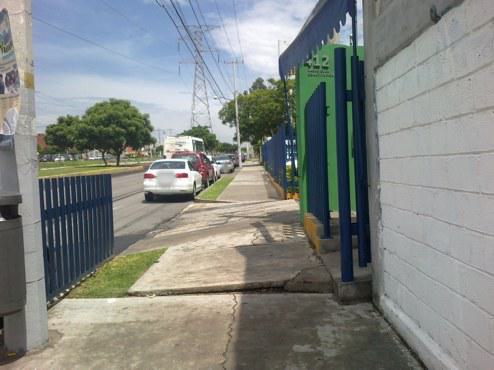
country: MX
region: Queretaro
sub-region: Queretaro
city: Sergio Villasenor
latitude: 20.6256
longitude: -100.4000
